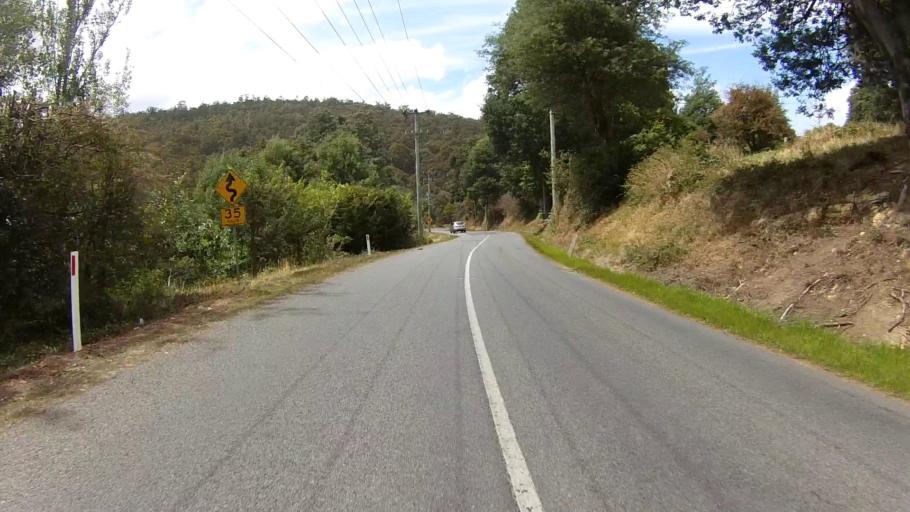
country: AU
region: Tasmania
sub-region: Kingborough
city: Kettering
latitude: -43.1043
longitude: 147.2221
